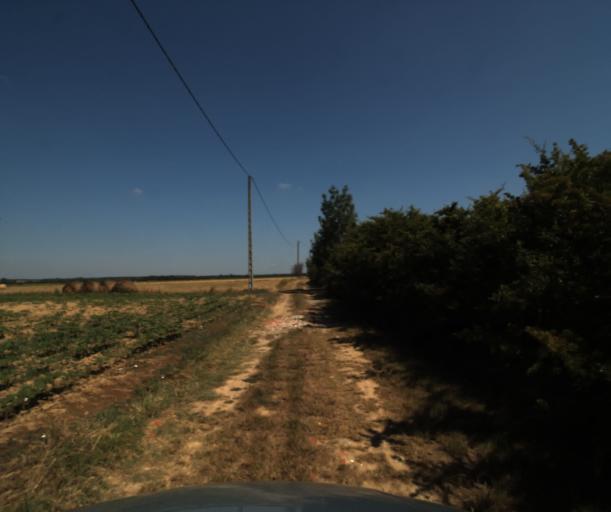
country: FR
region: Midi-Pyrenees
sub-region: Departement de la Haute-Garonne
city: Labastidette
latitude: 43.4717
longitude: 1.2405
